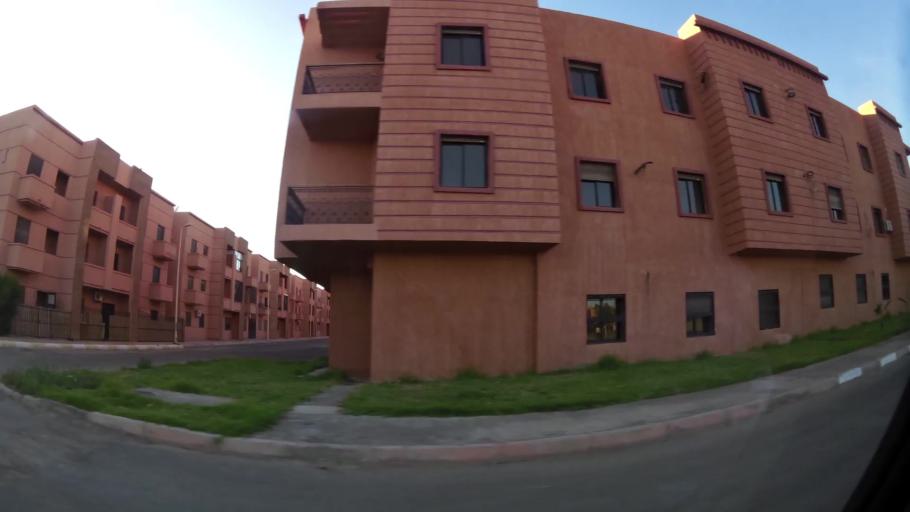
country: MA
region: Marrakech-Tensift-Al Haouz
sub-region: Marrakech
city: Marrakesh
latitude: 31.7480
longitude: -8.1088
